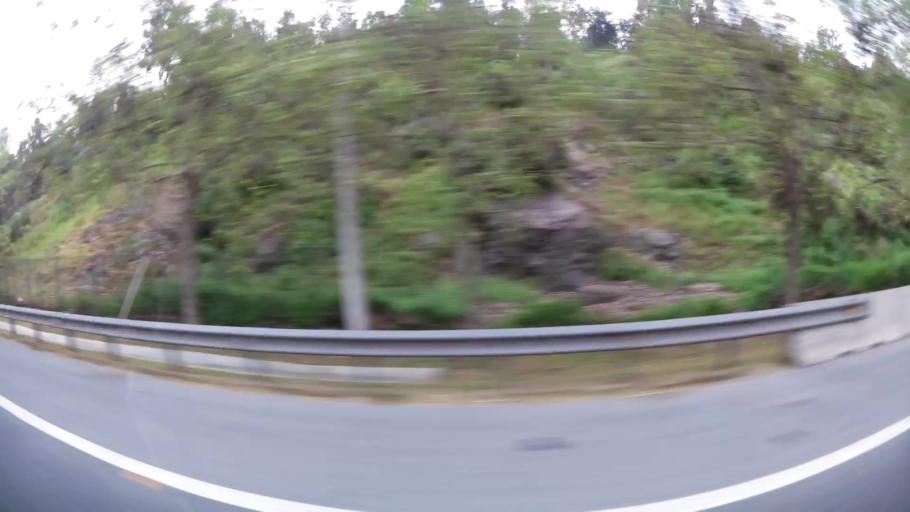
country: CL
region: Santiago Metropolitan
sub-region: Provincia de Santiago
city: Villa Presidente Frei, Nunoa, Santiago, Chile
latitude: -33.3940
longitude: -70.6033
